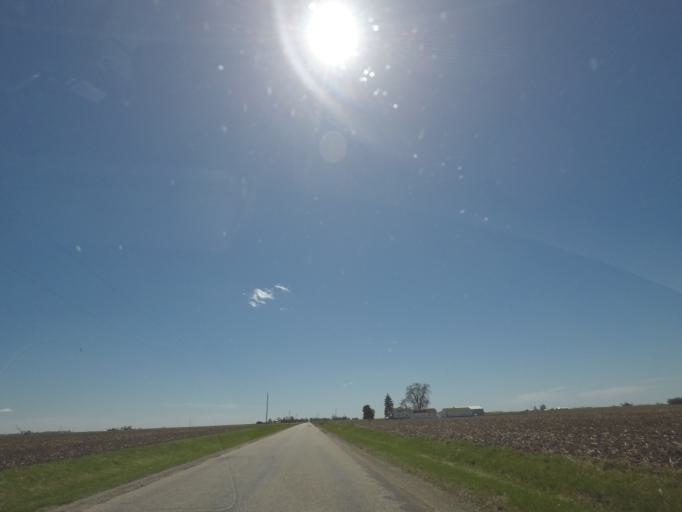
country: US
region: Illinois
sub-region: Logan County
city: Atlanta
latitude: 40.1680
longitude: -89.1937
